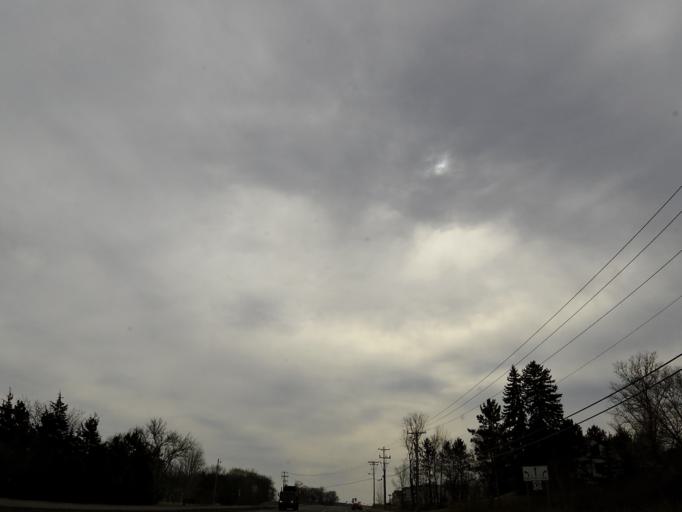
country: US
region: Minnesota
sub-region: Dakota County
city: Inver Grove Heights
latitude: 44.8347
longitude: -93.0226
